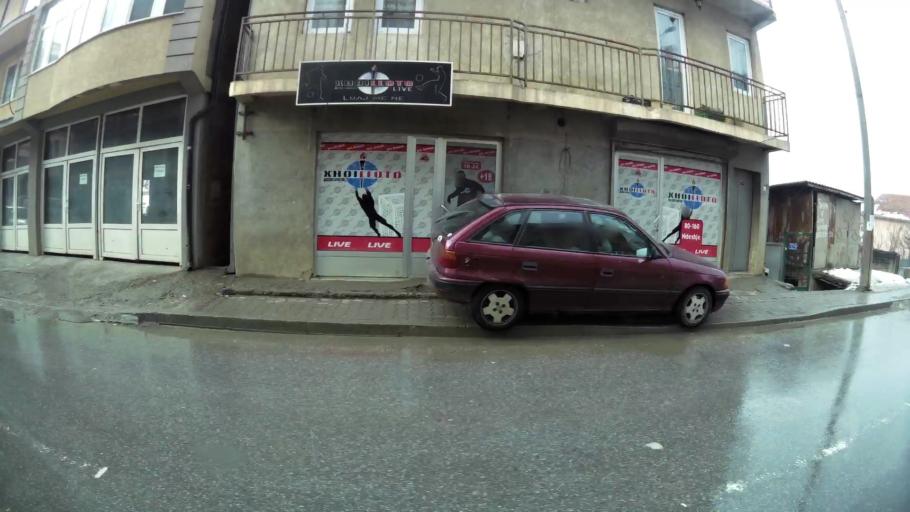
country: XK
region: Pristina
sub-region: Komuna e Prishtines
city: Pristina
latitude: 42.6732
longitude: 21.1730
